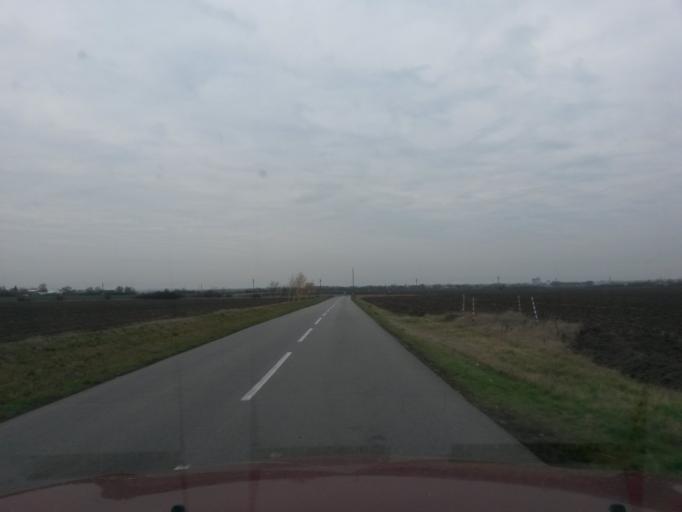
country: SK
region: Kosicky
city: Trebisov
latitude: 48.6379
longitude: 21.6754
